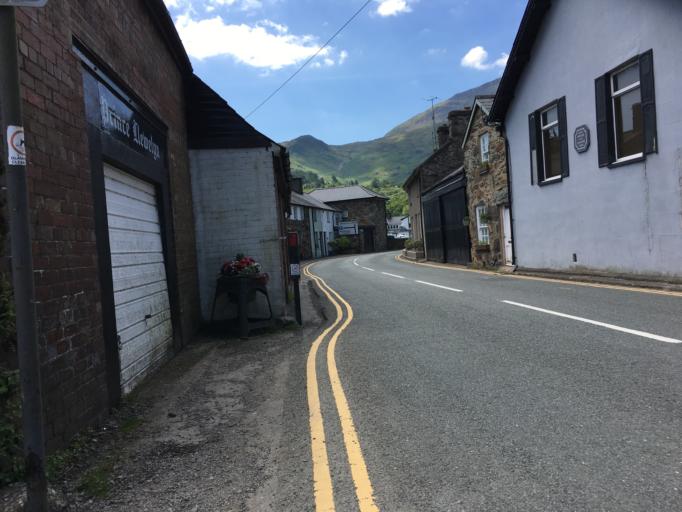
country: GB
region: Wales
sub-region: Gwynedd
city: Penrhyndeudraeth
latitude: 53.0122
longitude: -4.1009
